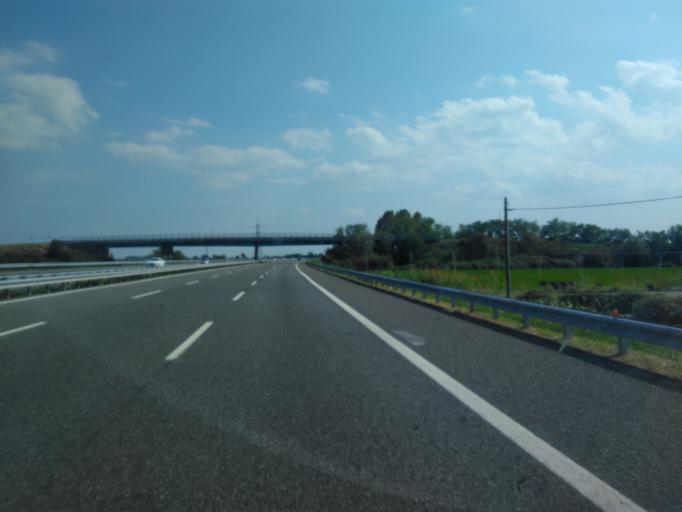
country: IT
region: Piedmont
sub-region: Provincia di Vercelli
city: Prarolo
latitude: 45.2814
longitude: 8.4714
